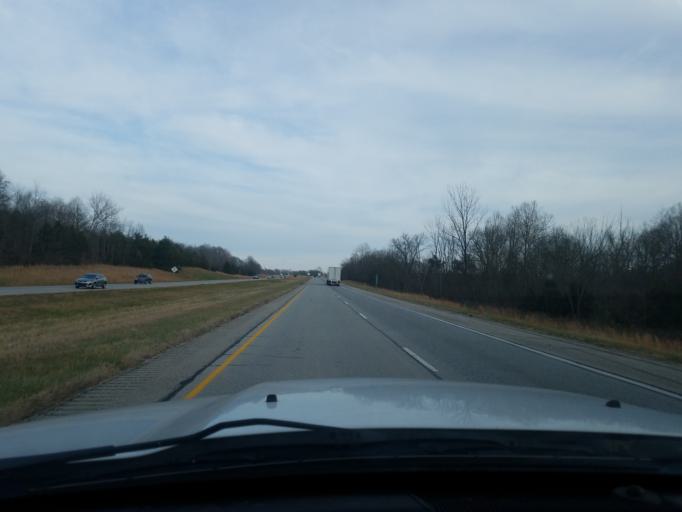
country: US
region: Indiana
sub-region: Harrison County
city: Corydon
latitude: 38.2467
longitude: -86.0818
